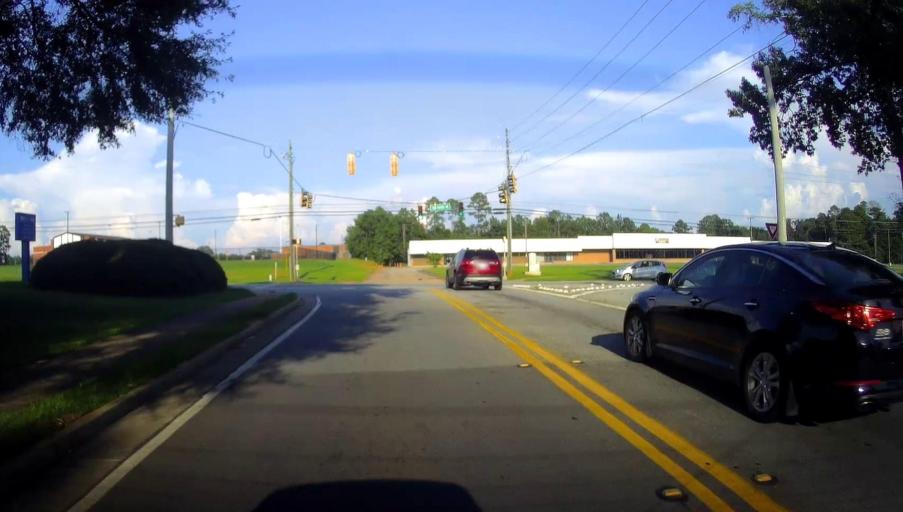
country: US
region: Georgia
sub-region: Houston County
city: Perry
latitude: 32.4685
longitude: -83.7290
